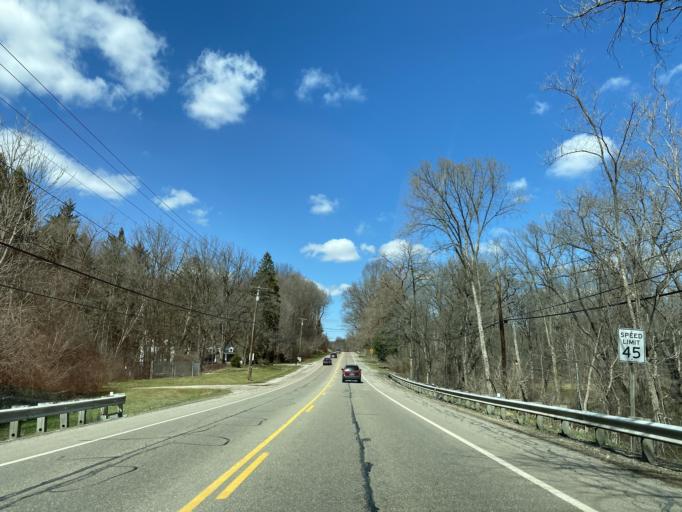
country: US
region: Ohio
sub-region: Summit County
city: Montrose-Ghent
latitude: 41.1726
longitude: -81.6368
